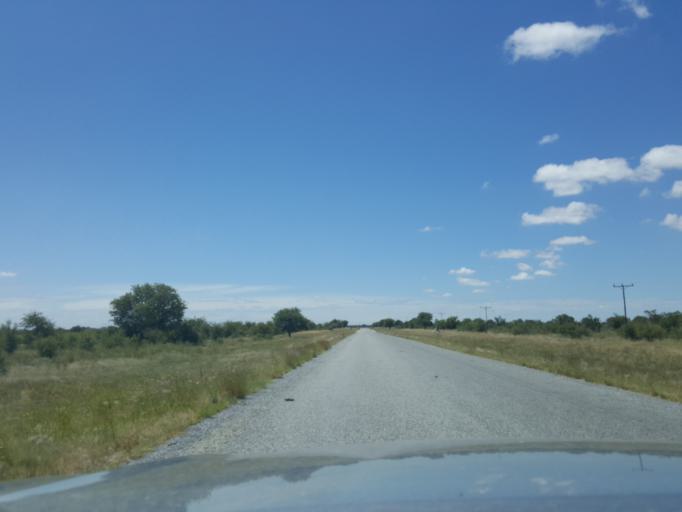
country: BW
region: Central
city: Nata
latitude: -20.1557
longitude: 25.8290
